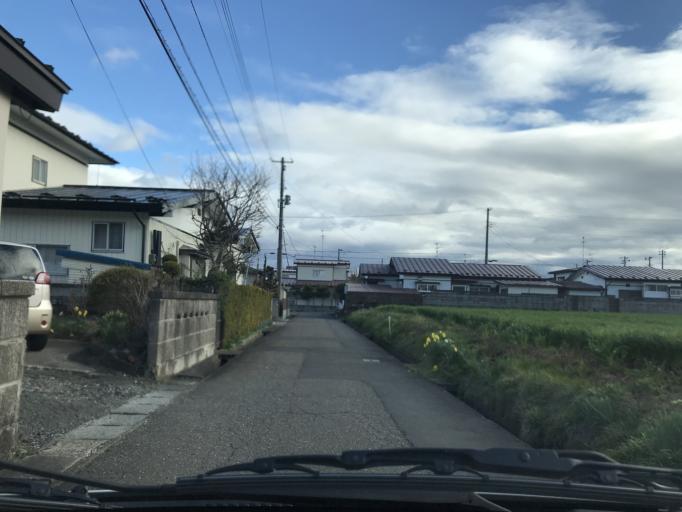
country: JP
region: Iwate
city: Mizusawa
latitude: 39.1136
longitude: 141.1406
